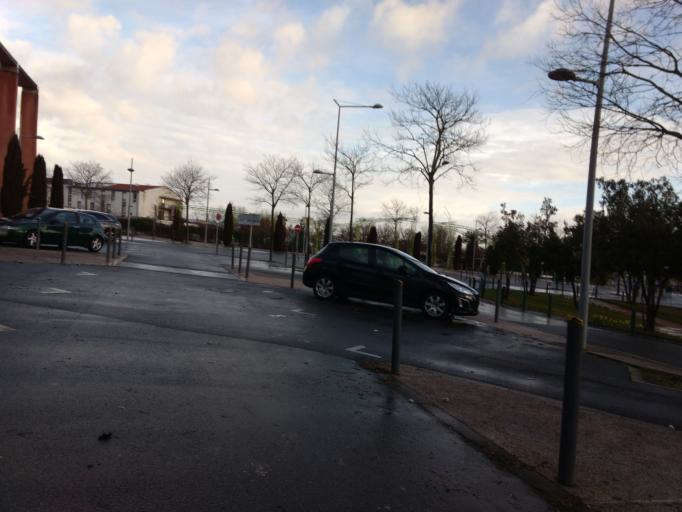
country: FR
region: Midi-Pyrenees
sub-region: Departement de la Haute-Garonne
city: Tournefeuille
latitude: 43.6001
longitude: 1.3227
